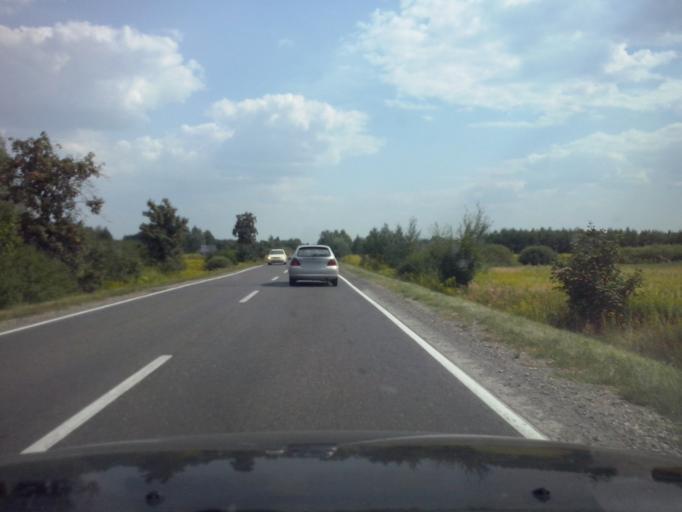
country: PL
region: Subcarpathian Voivodeship
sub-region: Powiat nizanski
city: Przedzel
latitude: 50.4746
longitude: 22.2330
